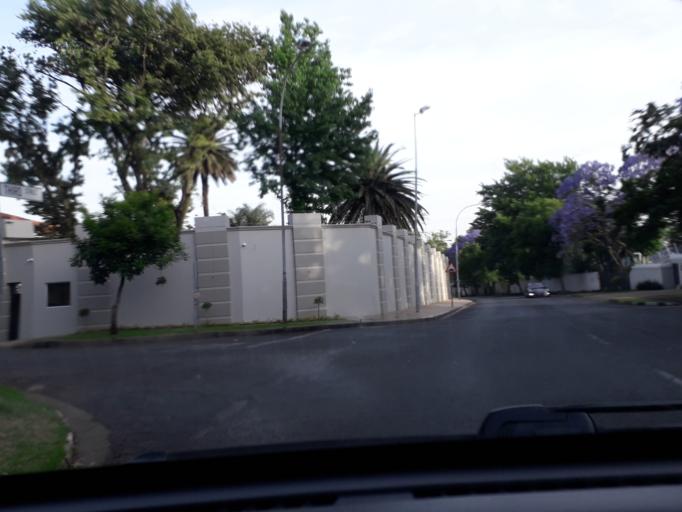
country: ZA
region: Gauteng
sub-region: City of Johannesburg Metropolitan Municipality
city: Johannesburg
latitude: -26.1520
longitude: 28.0642
